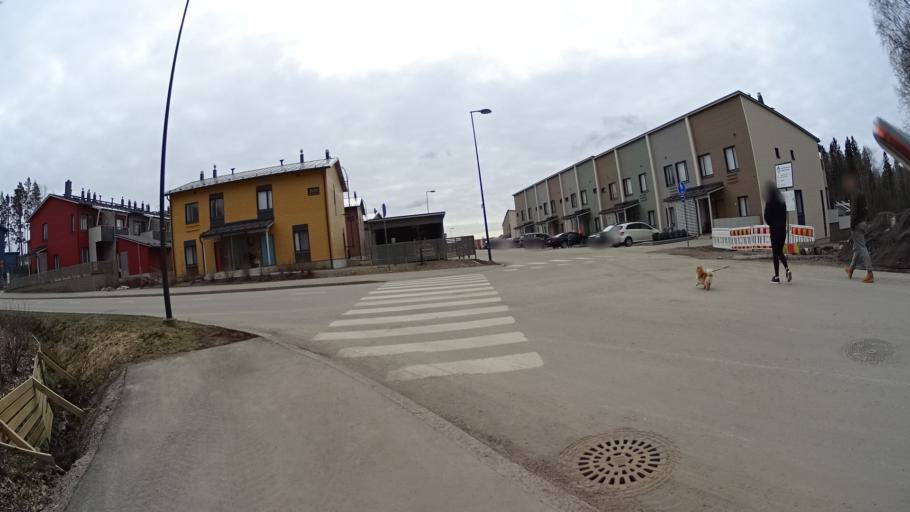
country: FI
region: Uusimaa
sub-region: Helsinki
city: Vantaa
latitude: 60.2936
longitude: 24.9407
